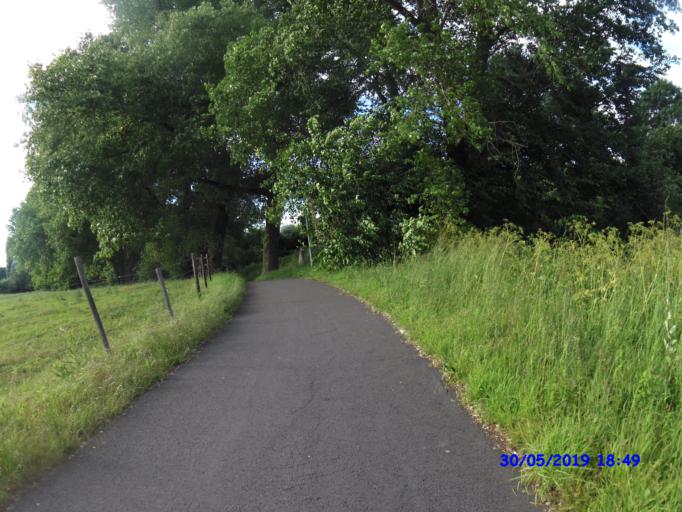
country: BE
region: Flanders
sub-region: Provincie West-Vlaanderen
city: Kortrijk
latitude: 50.8091
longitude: 3.2397
